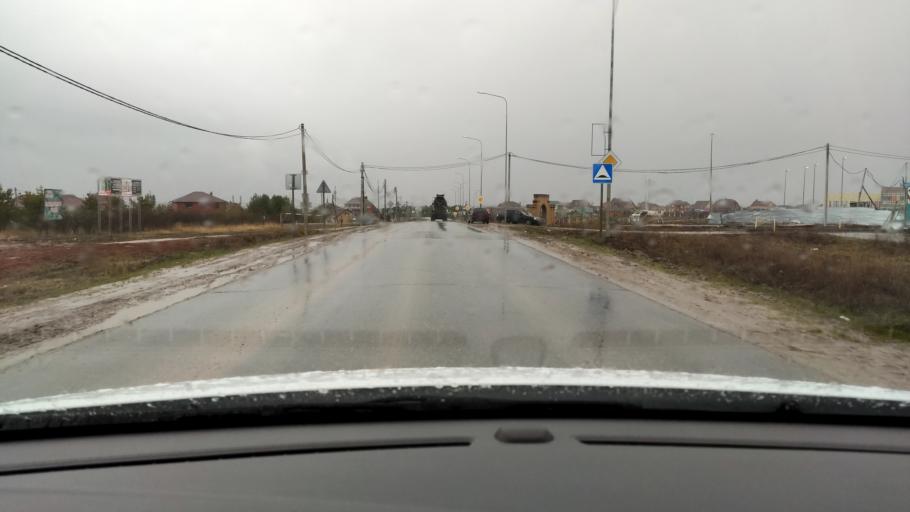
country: RU
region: Tatarstan
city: Vysokaya Gora
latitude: 55.9018
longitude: 49.3246
